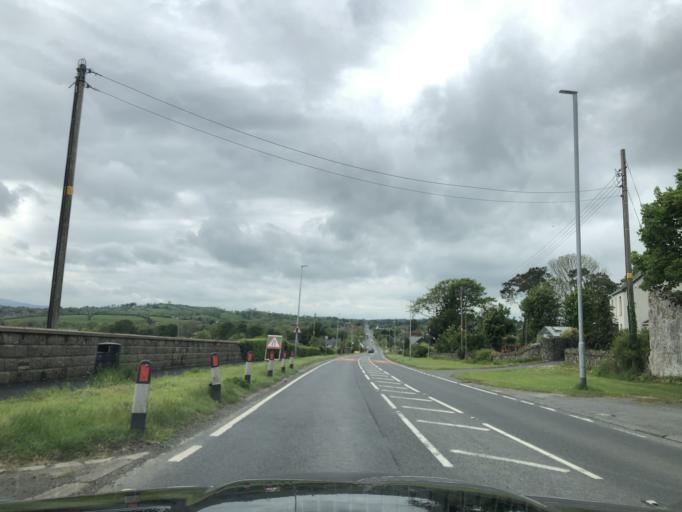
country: GB
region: Northern Ireland
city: Crossgar
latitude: 54.3615
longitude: -5.7654
